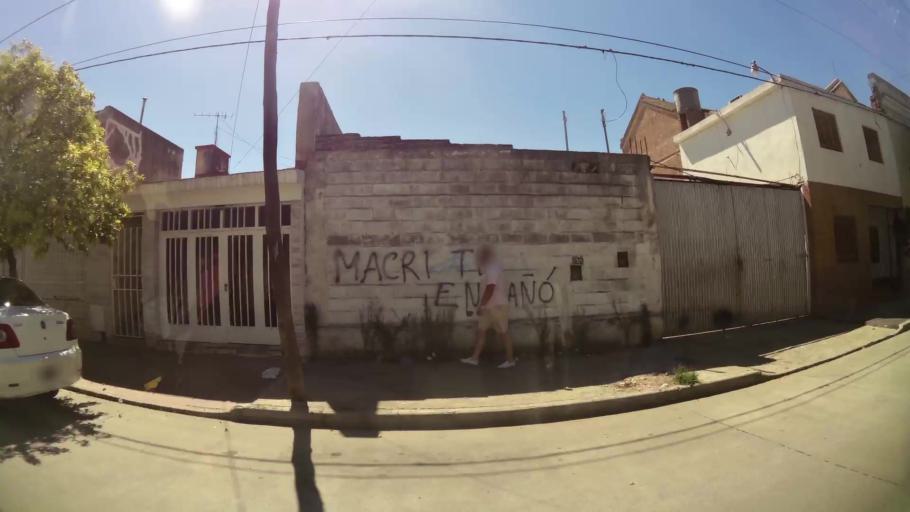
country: AR
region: Cordoba
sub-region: Departamento de Capital
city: Cordoba
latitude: -31.4226
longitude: -64.1492
